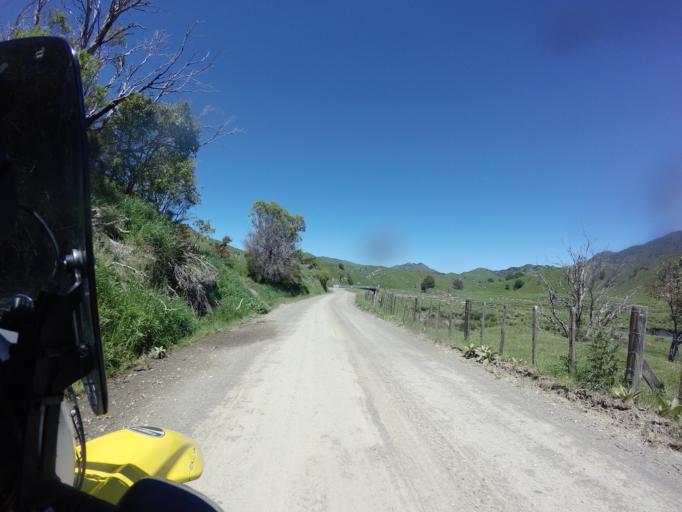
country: NZ
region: Bay of Plenty
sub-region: Opotiki District
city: Opotiki
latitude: -38.3886
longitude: 177.4606
